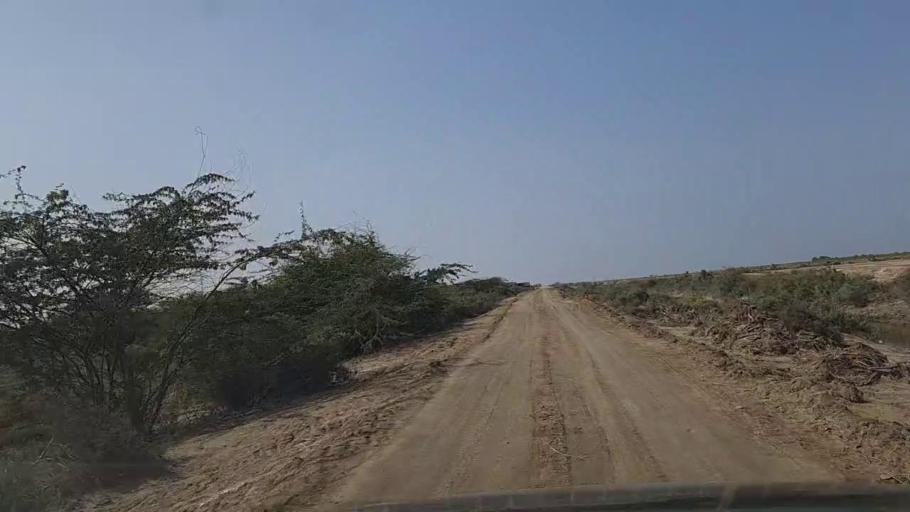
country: PK
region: Sindh
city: Gharo
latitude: 24.7074
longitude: 67.5443
